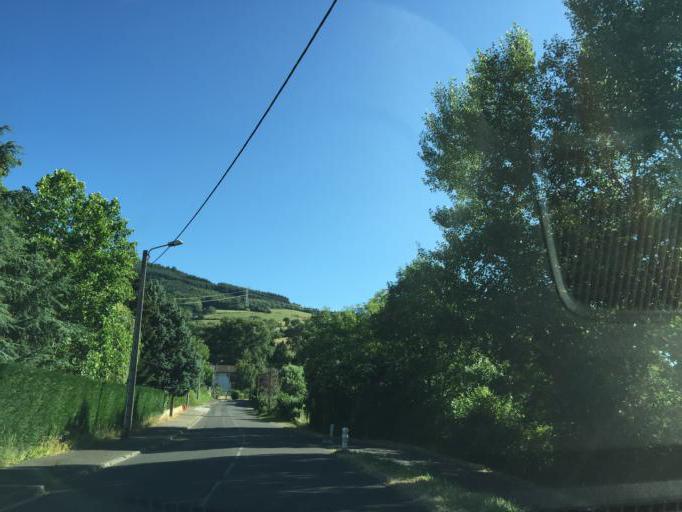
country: FR
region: Rhone-Alpes
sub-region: Departement de la Loire
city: Saint-Jean-Bonnefonds
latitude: 45.4409
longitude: 4.4698
